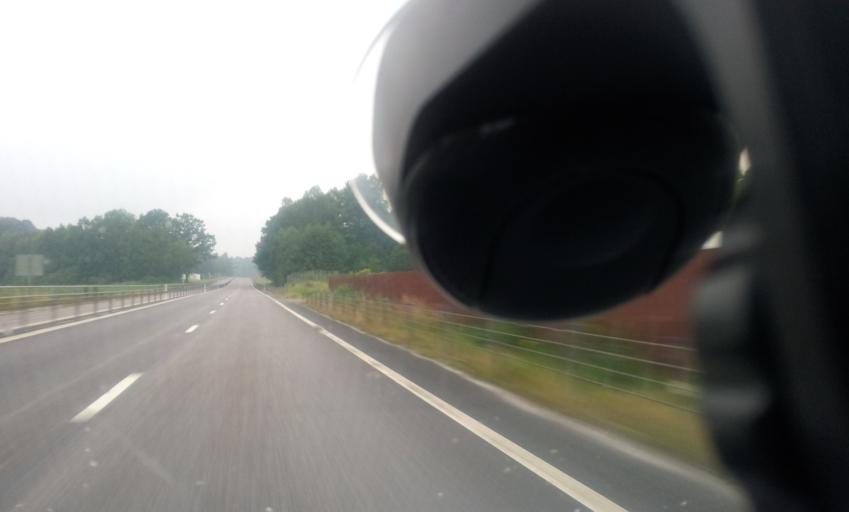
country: SE
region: Kalmar
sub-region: Vasterviks Kommun
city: Vaestervik
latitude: 57.8040
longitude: 16.5062
